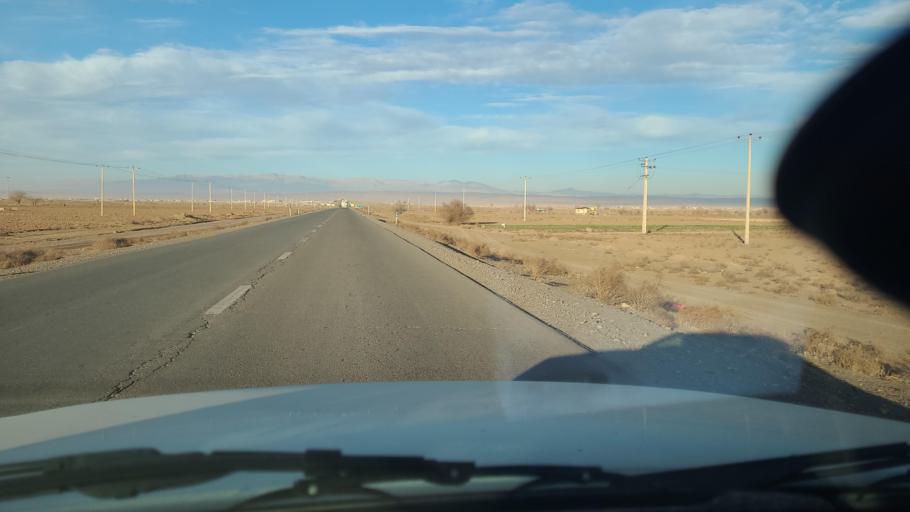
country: IR
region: Razavi Khorasan
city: Neqab
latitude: 36.5945
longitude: 57.5864
